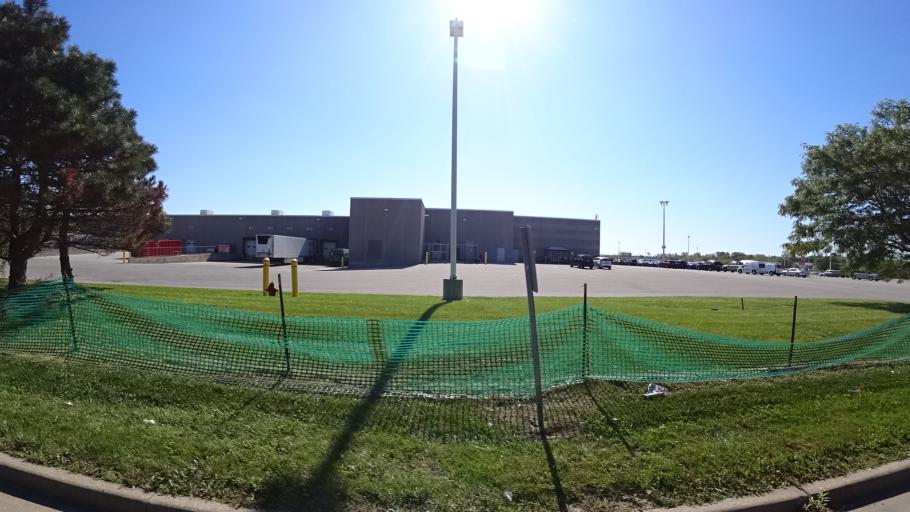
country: US
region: Indiana
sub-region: LaPorte County
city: Michigan City
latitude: 41.6766
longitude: -86.8904
